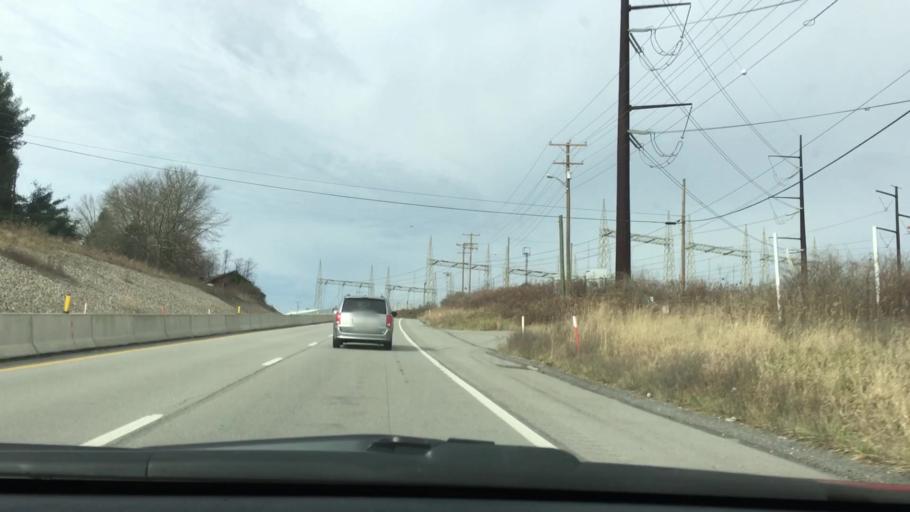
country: US
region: Pennsylvania
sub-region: Fayette County
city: Masontown
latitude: 39.8555
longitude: -79.9306
